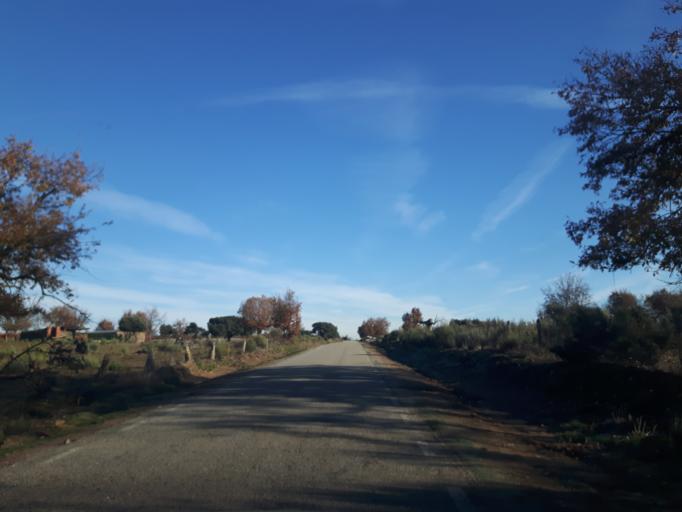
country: ES
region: Castille and Leon
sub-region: Provincia de Salamanca
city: Cerralbo
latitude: 40.9490
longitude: -6.6071
